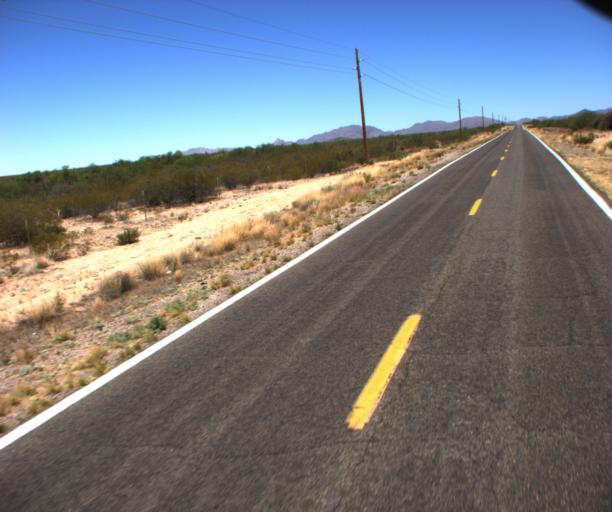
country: US
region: Arizona
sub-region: Yavapai County
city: Congress
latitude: 34.0718
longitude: -112.8218
